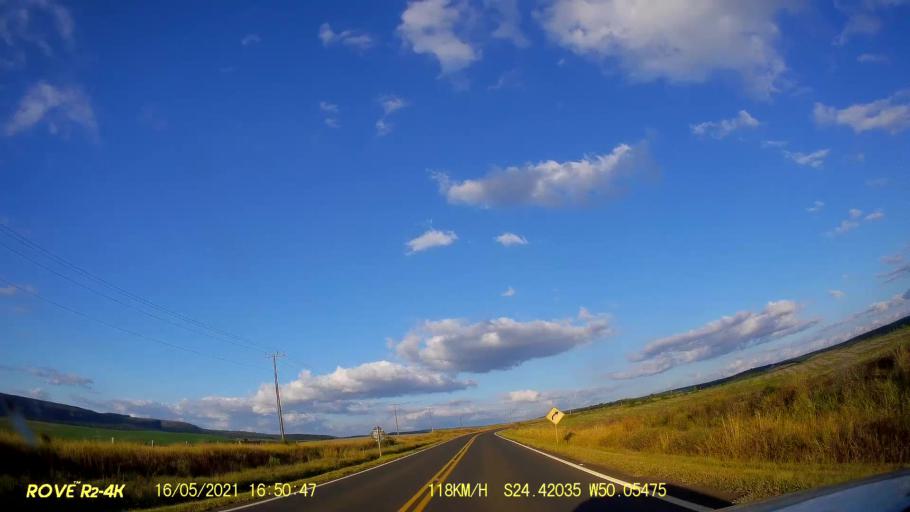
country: BR
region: Parana
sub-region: Pirai Do Sul
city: Pirai do Sul
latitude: -24.4204
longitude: -50.0546
